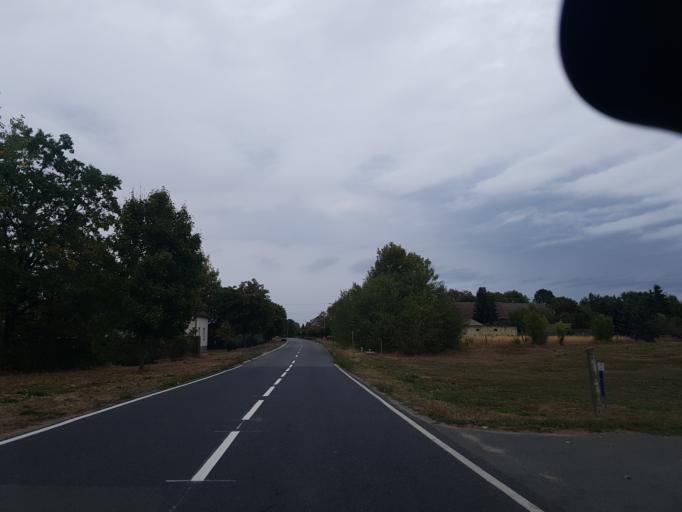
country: DE
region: Saxony-Anhalt
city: Prettin
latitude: 51.6977
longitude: 12.8873
